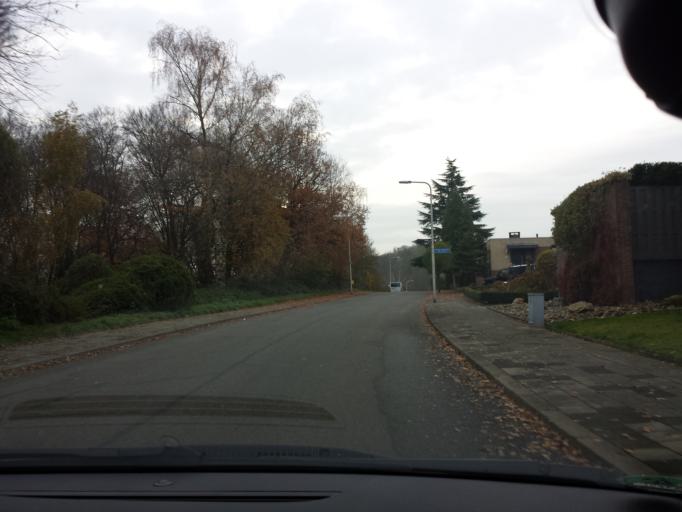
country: NL
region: Limburg
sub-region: Gemeente Kerkrade
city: Kerkrade
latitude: 50.8812
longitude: 6.0762
